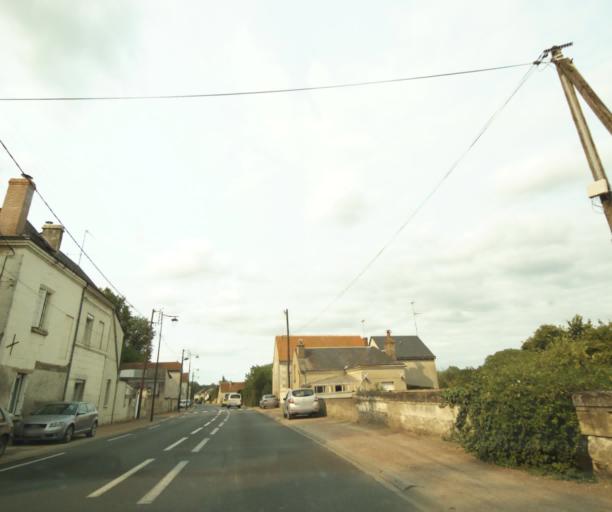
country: FR
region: Centre
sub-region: Departement d'Indre-et-Loire
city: Loches
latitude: 47.1423
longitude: 1.0012
